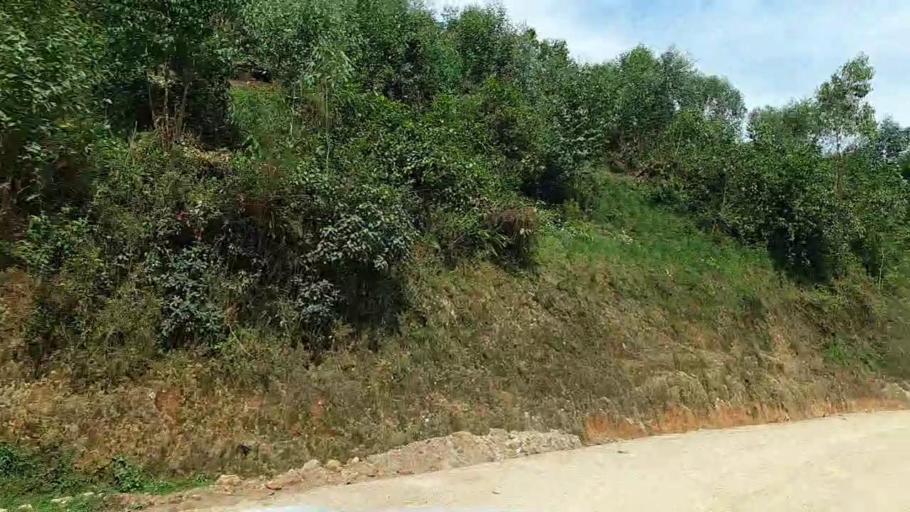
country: RW
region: Southern Province
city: Nzega
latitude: -2.3408
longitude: 29.4365
